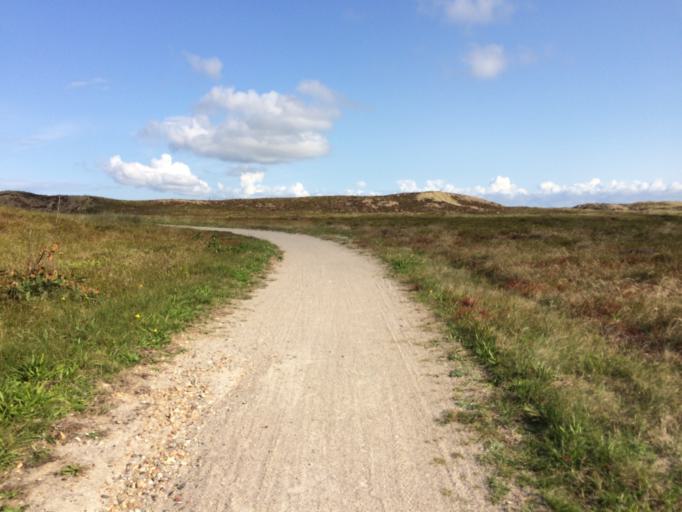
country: DK
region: Central Jutland
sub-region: Ringkobing-Skjern Kommune
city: Hvide Sande
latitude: 55.8934
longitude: 8.1685
